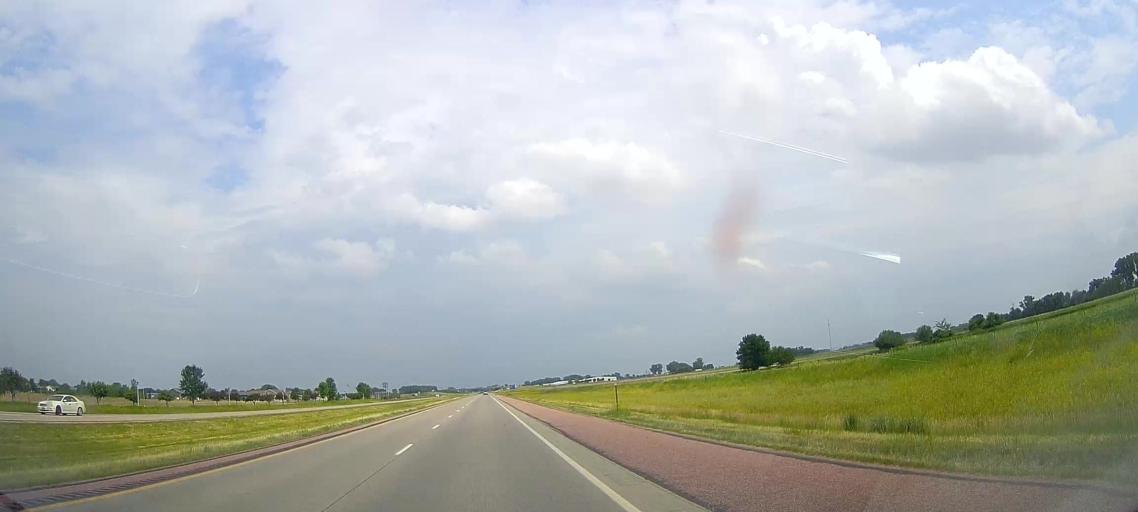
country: US
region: South Dakota
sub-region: Union County
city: Elk Point
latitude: 42.6723
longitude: -96.6781
